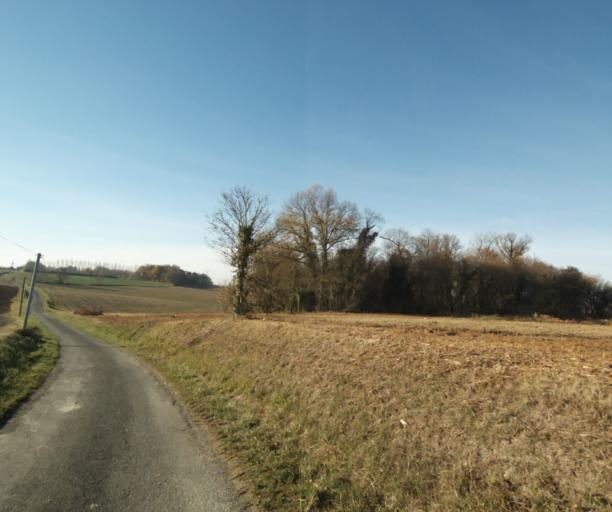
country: FR
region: Poitou-Charentes
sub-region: Departement de la Charente-Maritime
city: Fontcouverte
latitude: 45.7412
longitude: -0.5845
